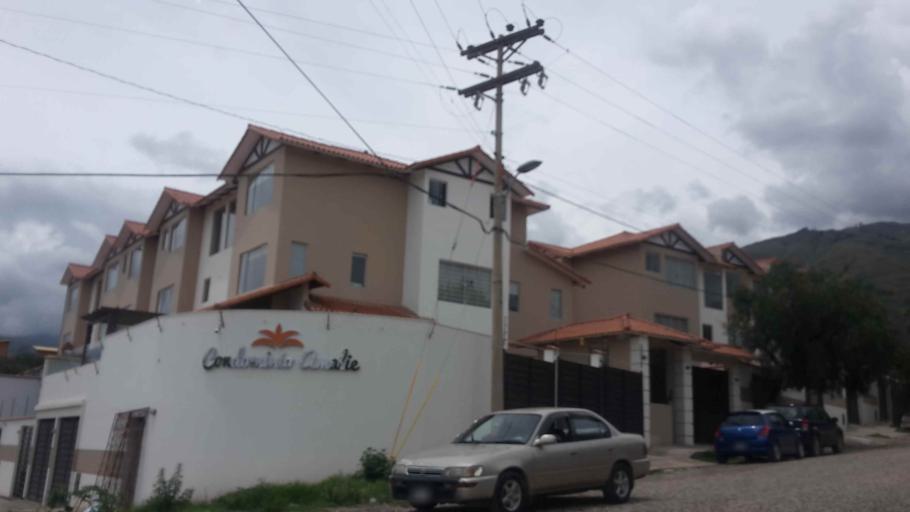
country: BO
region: Cochabamba
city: Cochabamba
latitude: -17.3400
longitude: -66.1882
